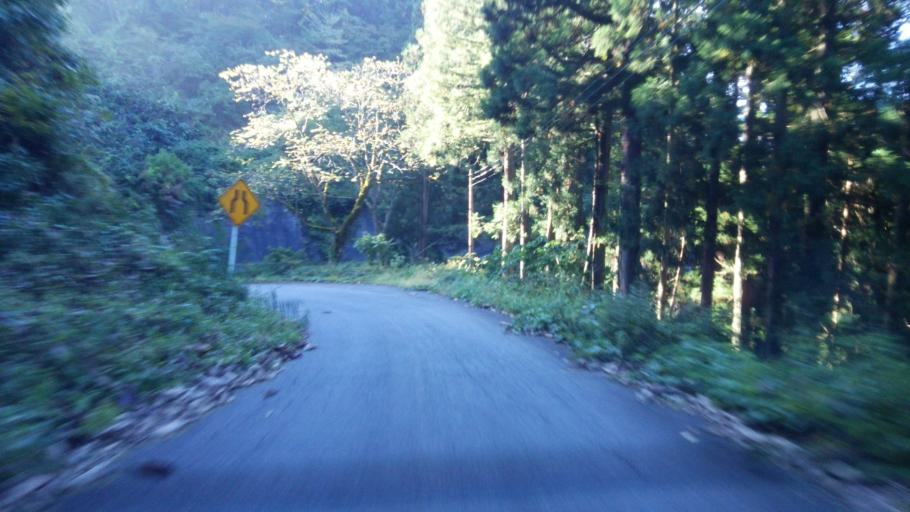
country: JP
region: Fukushima
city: Kitakata
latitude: 37.4620
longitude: 139.7255
